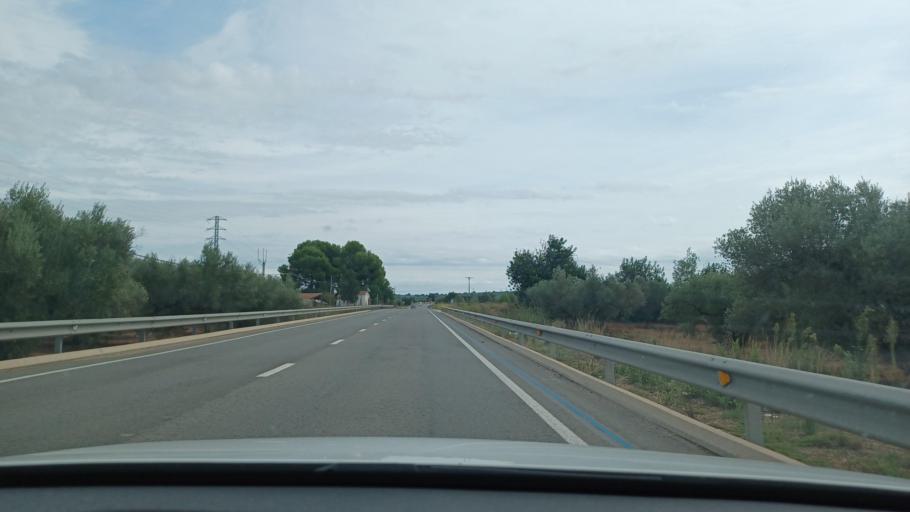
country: ES
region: Catalonia
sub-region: Provincia de Tarragona
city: Masdenverge
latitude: 40.7171
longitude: 0.5125
